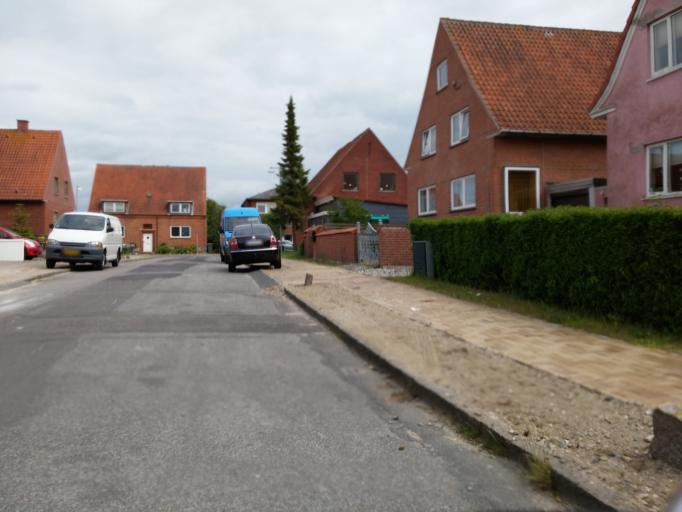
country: DK
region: South Denmark
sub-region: Odense Kommune
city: Odense
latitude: 55.4086
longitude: 10.4064
